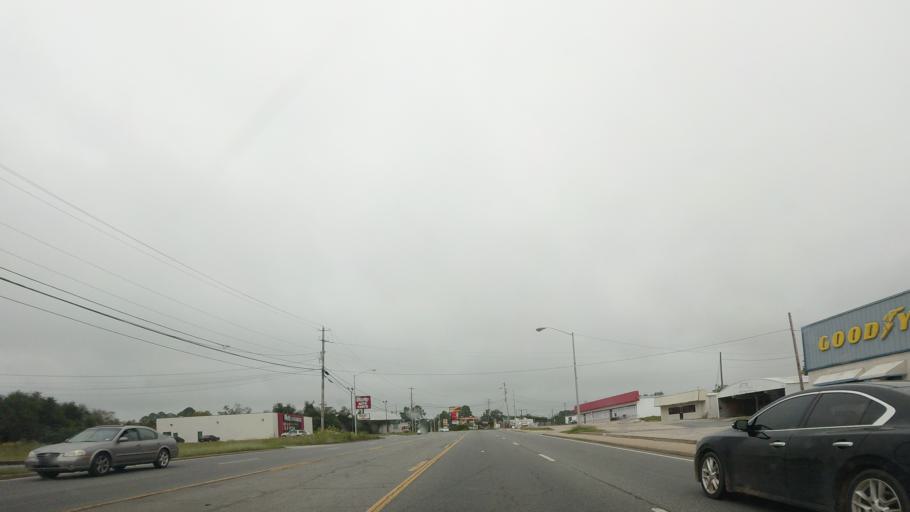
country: US
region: Georgia
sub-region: Ben Hill County
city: Fitzgerald
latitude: 31.7033
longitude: -83.2524
